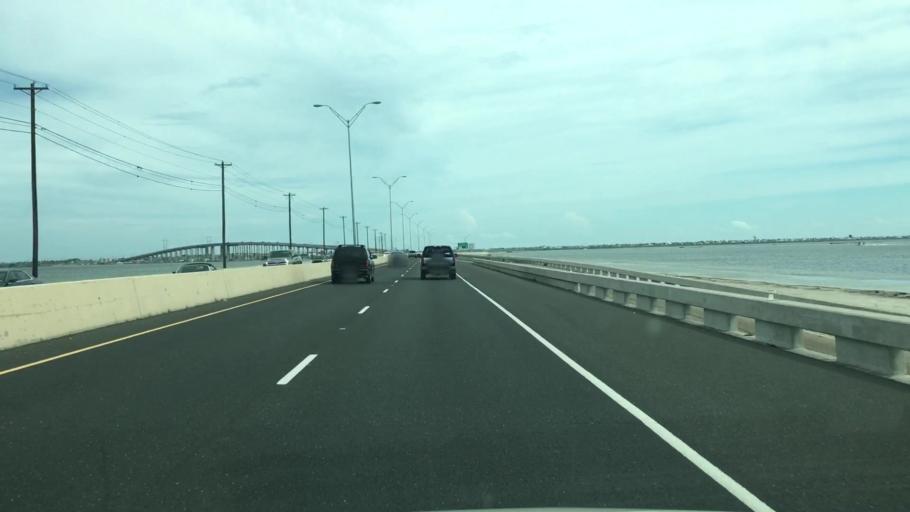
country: US
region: Texas
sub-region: Nueces County
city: Corpus Christi
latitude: 27.6435
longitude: -97.2492
